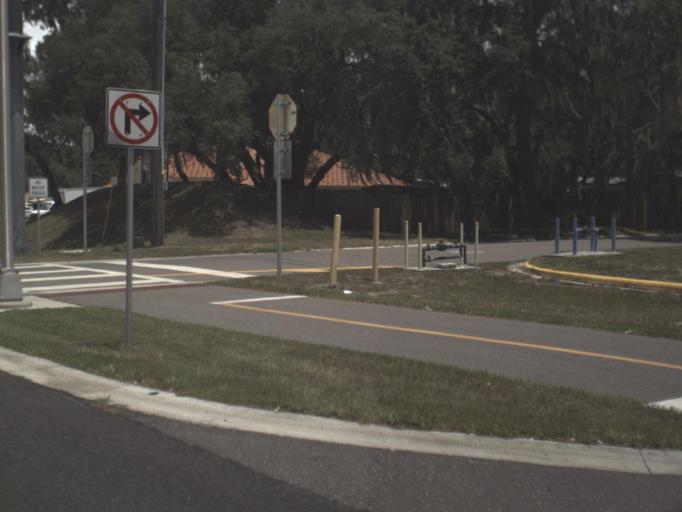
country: US
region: Florida
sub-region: Hillsborough County
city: Riverview
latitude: 27.8480
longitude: -82.3266
